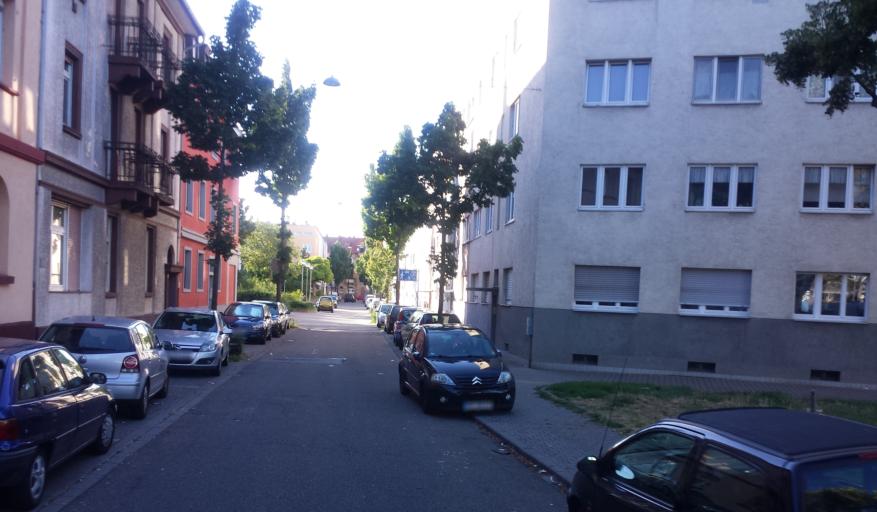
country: DE
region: Baden-Wuerttemberg
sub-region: Karlsruhe Region
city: Mannheim
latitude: 49.5267
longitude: 8.4812
